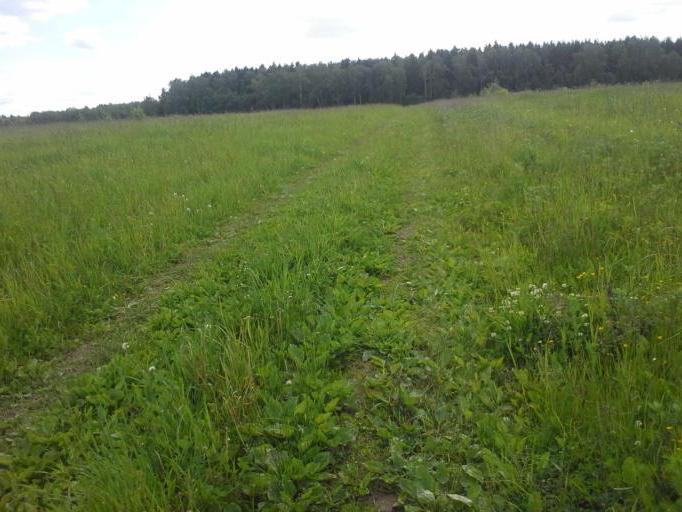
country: RU
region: Moskovskaya
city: Filimonki
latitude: 55.5584
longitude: 37.3955
